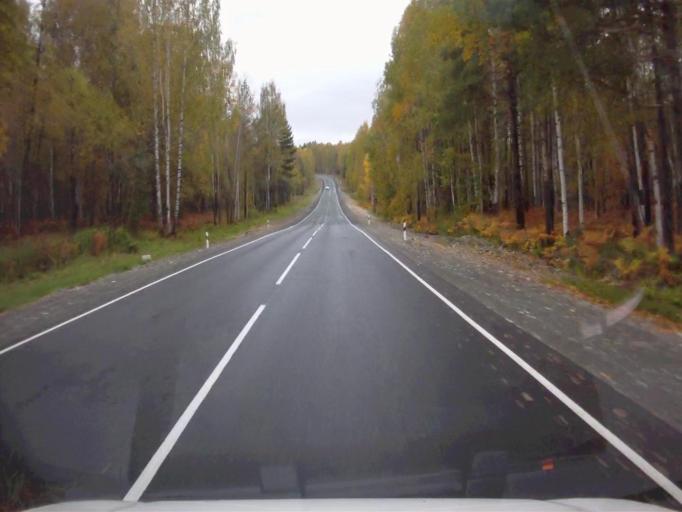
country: RU
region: Chelyabinsk
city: Nyazepetrovsk
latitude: 56.0645
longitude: 59.7187
